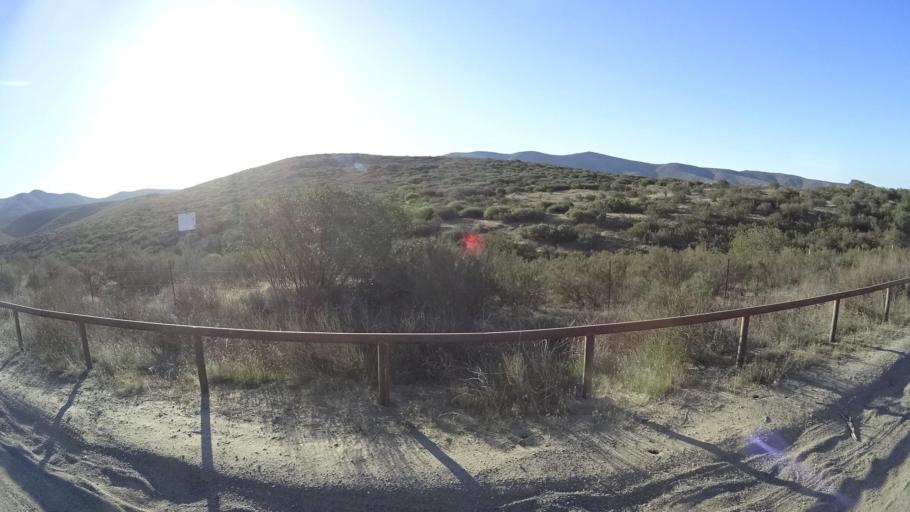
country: US
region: California
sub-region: San Diego County
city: Jamul
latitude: 32.6781
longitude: -116.9180
